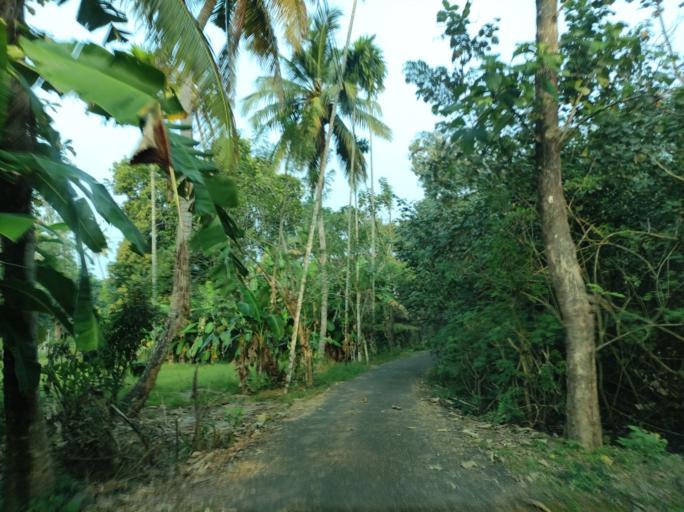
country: IN
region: Kerala
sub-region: Kottayam
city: Vaikam
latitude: 9.6802
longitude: 76.4662
